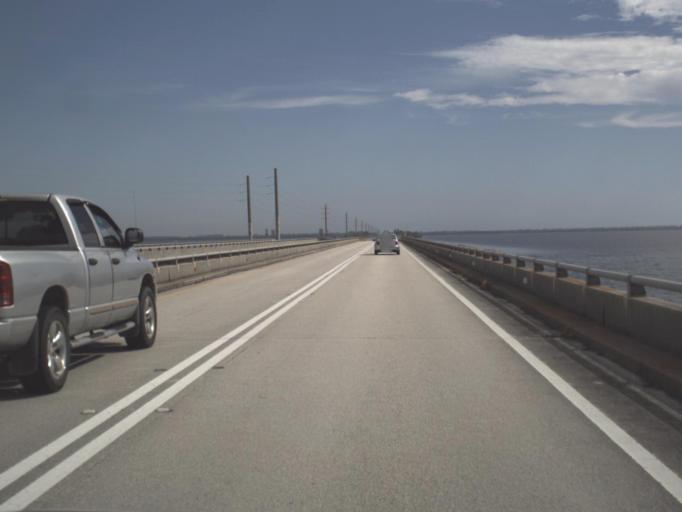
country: US
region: Florida
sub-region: Brevard County
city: Port Saint John
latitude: 28.5272
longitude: -80.7613
